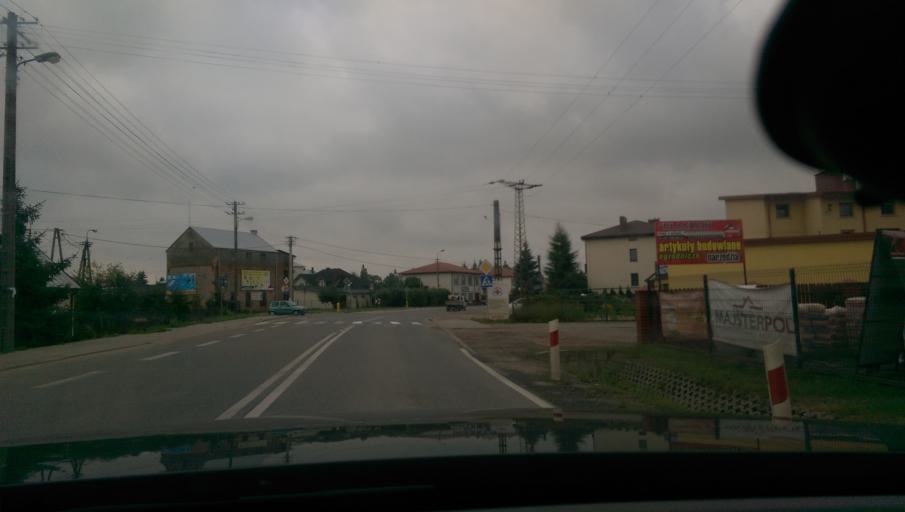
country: PL
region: Masovian Voivodeship
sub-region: Powiat przasnyski
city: Przasnysz
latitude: 53.0259
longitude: 20.8812
